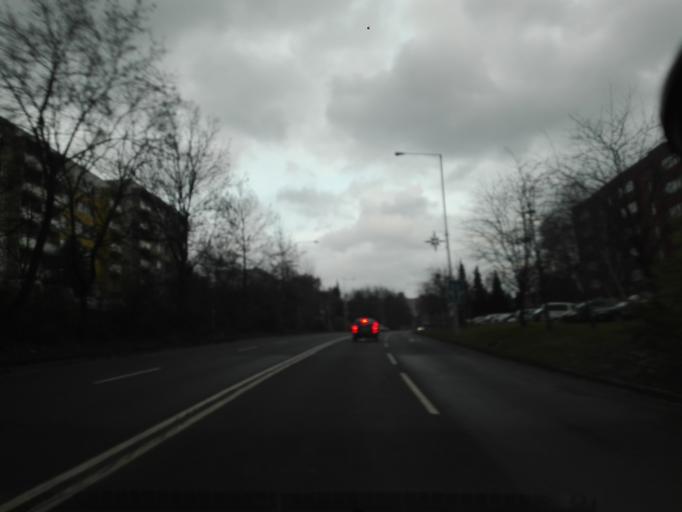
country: CZ
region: Moravskoslezsky
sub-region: Okres Frydek-Mistek
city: Frydek-Mistek
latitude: 49.6873
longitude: 18.3526
